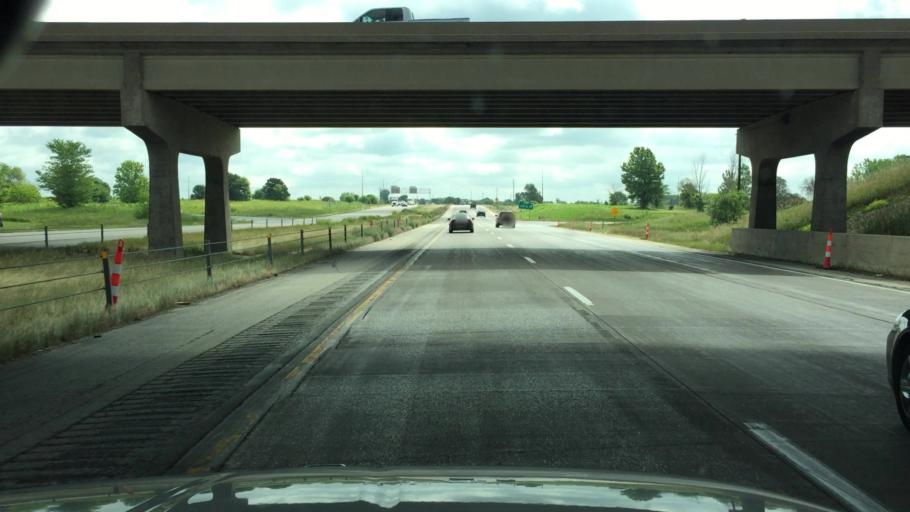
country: US
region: Iowa
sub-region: Scott County
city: Eldridge
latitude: 41.5961
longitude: -90.5702
